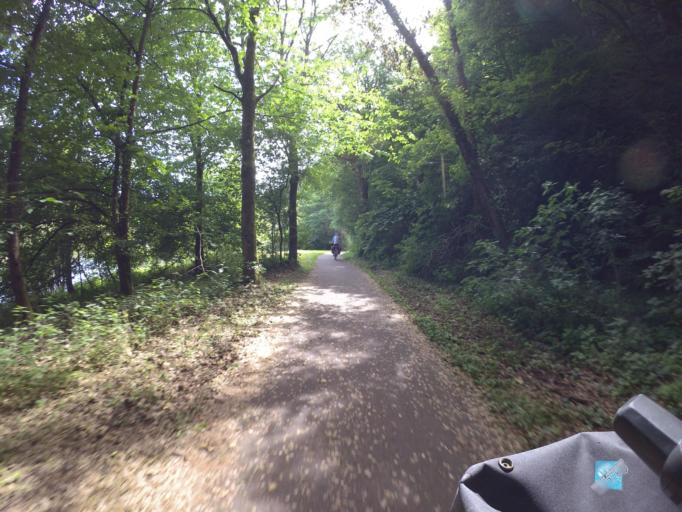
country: DE
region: Rheinland-Pfalz
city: Serrig
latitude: 49.5652
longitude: 6.5804
